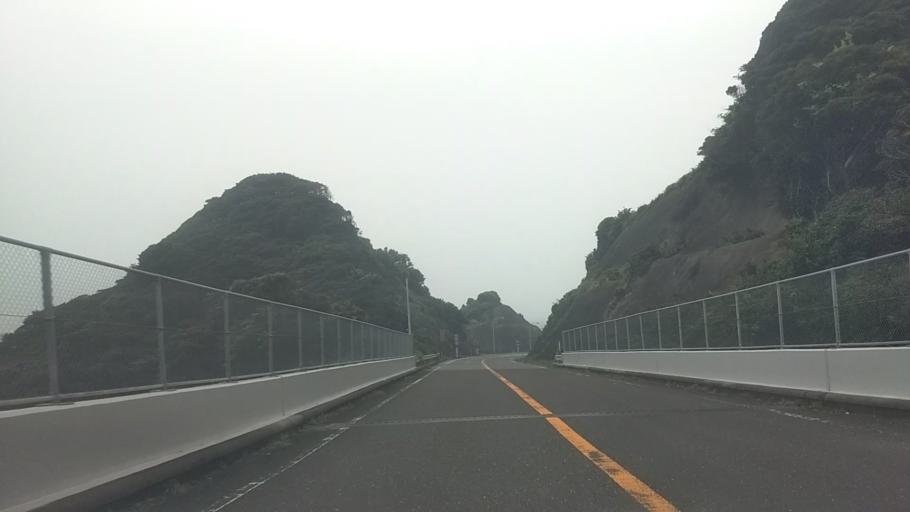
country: JP
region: Chiba
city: Katsuura
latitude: 35.1542
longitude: 140.3057
